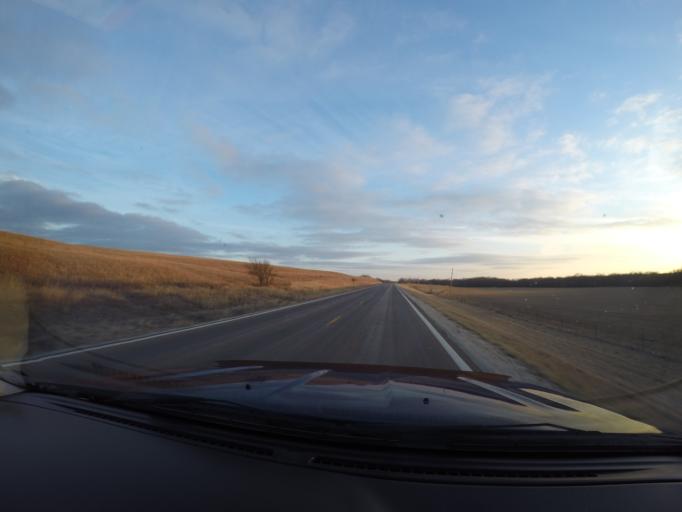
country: US
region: Kansas
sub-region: Chase County
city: Cottonwood Falls
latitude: 38.4765
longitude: -96.5566
